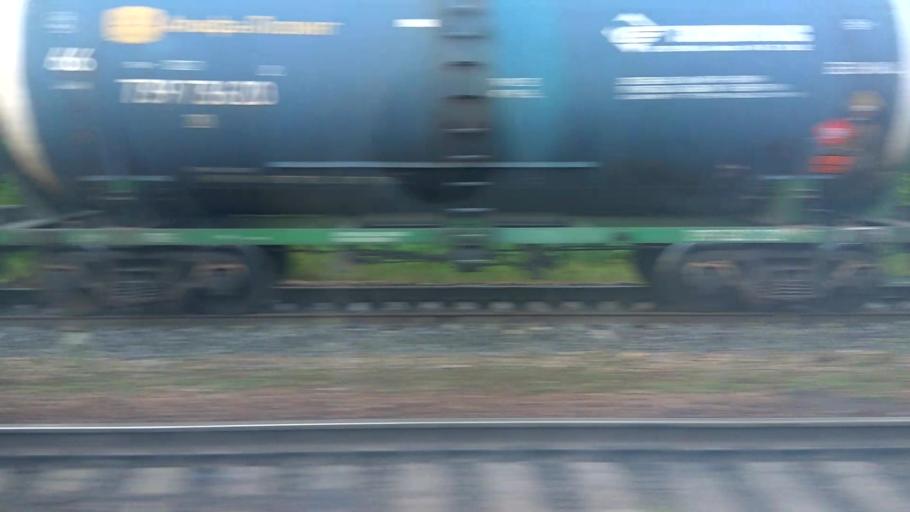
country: RU
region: Moskovskaya
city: Barybino
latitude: 55.2701
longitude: 37.8961
